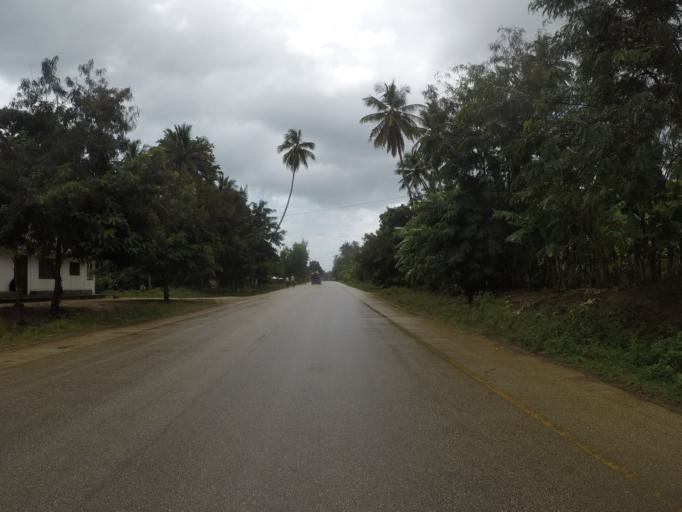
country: TZ
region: Zanzibar North
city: Mkokotoni
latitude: -5.9755
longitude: 39.1963
